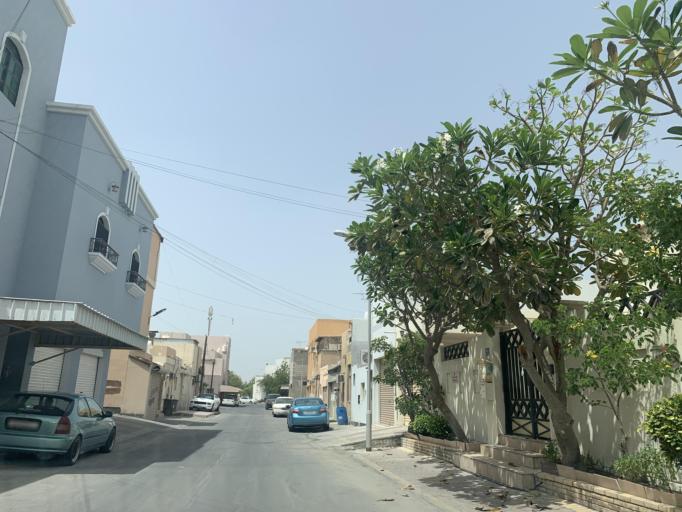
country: BH
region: Northern
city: Madinat `Isa
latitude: 26.1557
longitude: 50.5253
